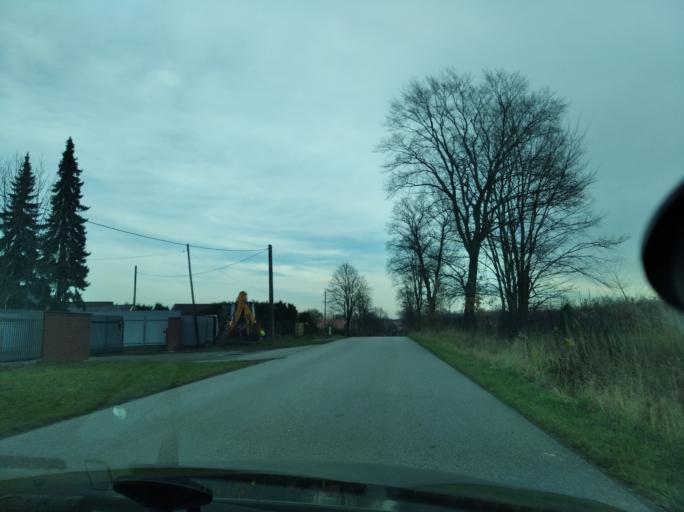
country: PL
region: Subcarpathian Voivodeship
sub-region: Powiat lancucki
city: Albigowa
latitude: 50.0347
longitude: 22.2250
